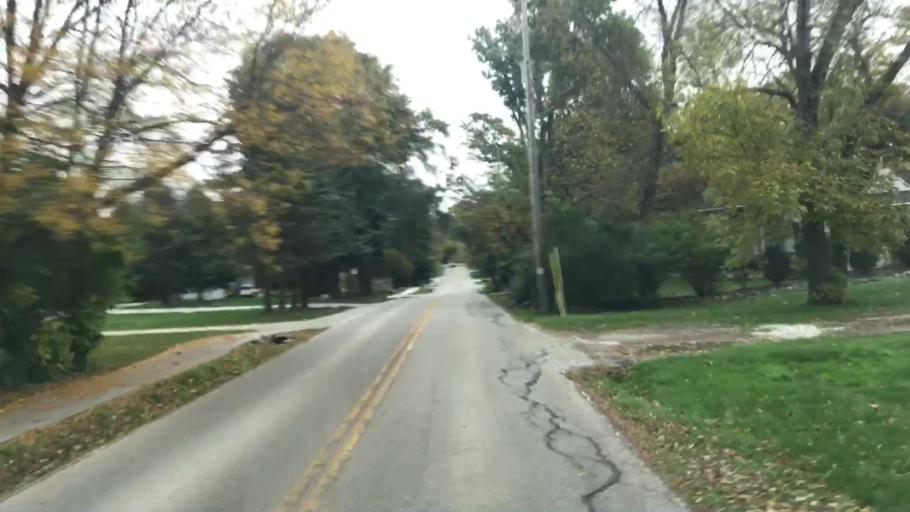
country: US
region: Wisconsin
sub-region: Waukesha County
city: Elm Grove
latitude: 43.0459
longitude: -88.0908
